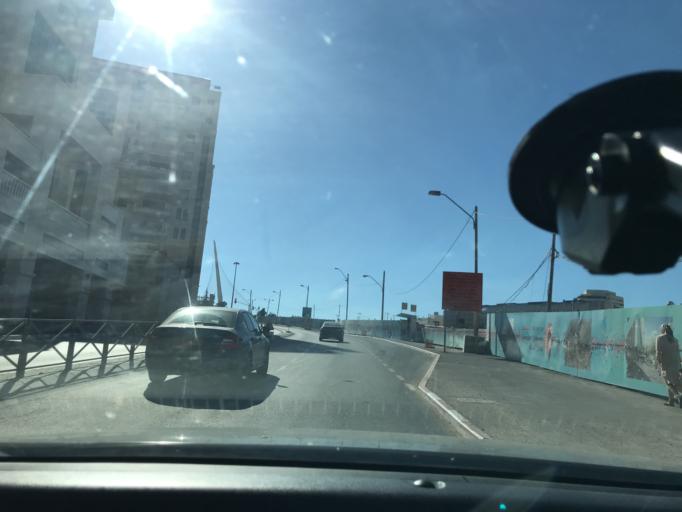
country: IL
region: Jerusalem
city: West Jerusalem
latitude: 31.7862
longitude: 35.2061
